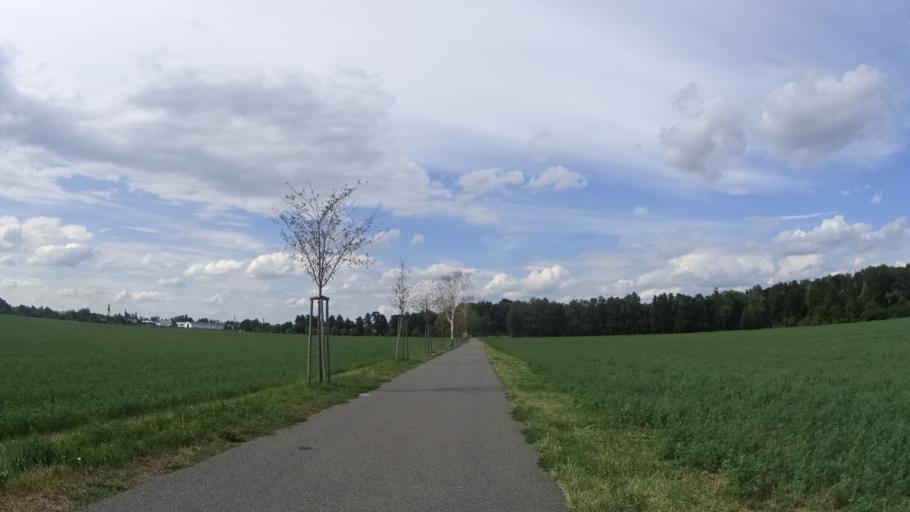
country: CZ
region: Olomoucky
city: Litovel
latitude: 49.6942
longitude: 17.0944
